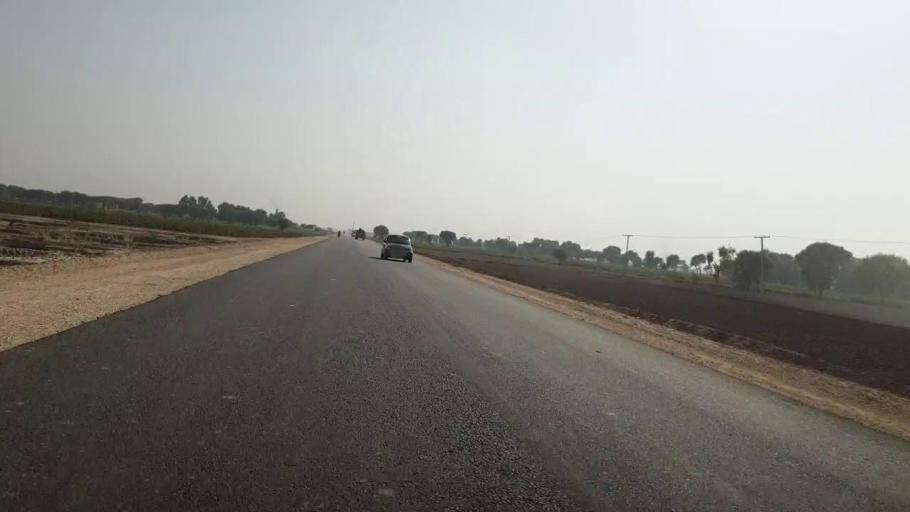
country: PK
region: Sindh
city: Dadu
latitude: 26.6655
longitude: 67.7765
